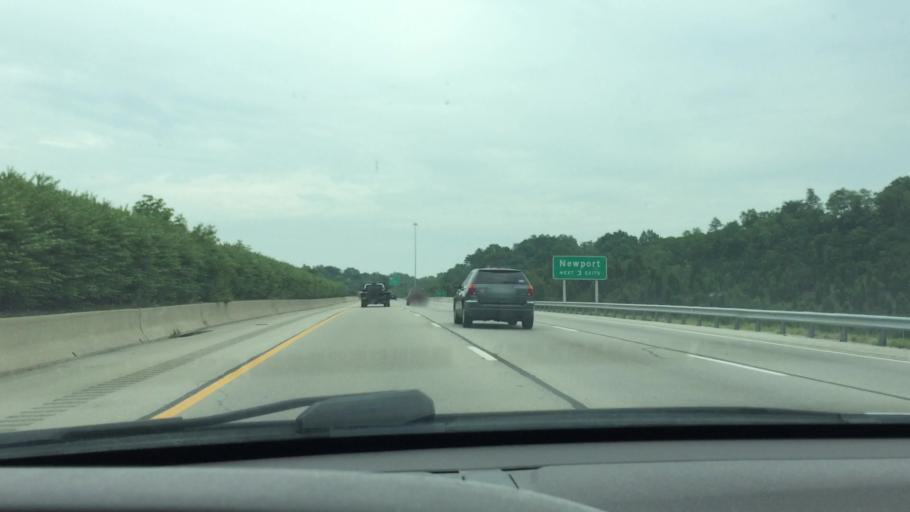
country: US
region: Kentucky
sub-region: Campbell County
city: Southgate
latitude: 39.0649
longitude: -84.4665
